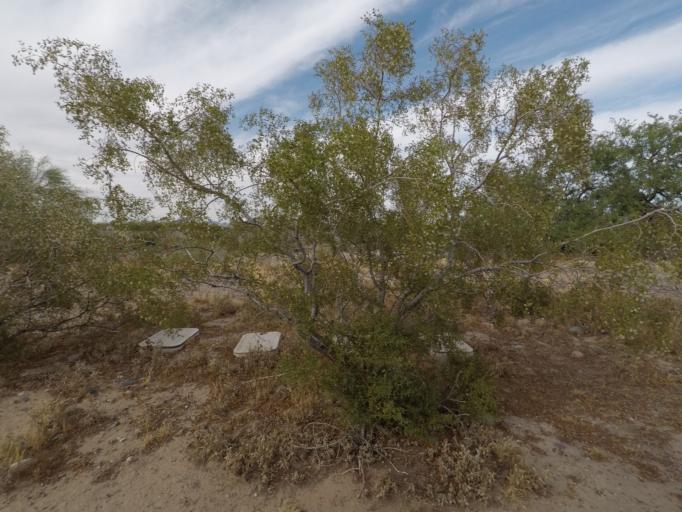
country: US
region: Arizona
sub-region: Maricopa County
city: Phoenix
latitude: 33.4188
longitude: -112.0559
